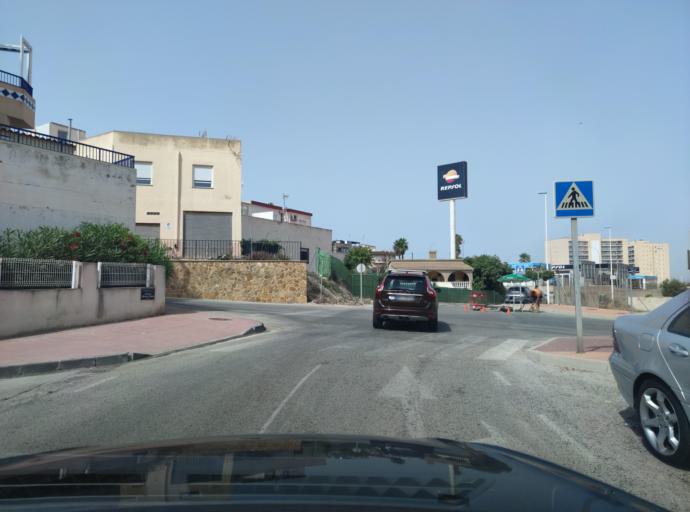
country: ES
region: Valencia
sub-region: Provincia de Alicante
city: Guardamar del Segura
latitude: 38.0958
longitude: -0.6575
